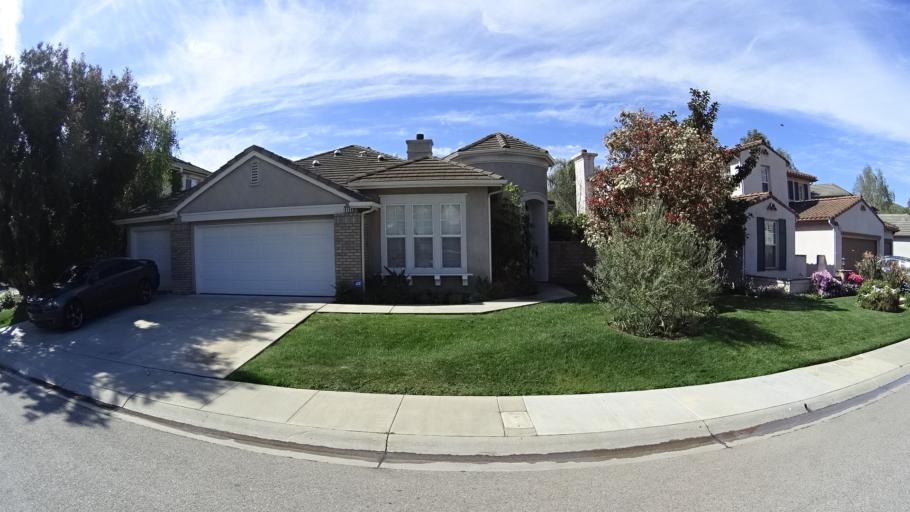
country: US
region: California
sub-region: Ventura County
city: Casa Conejo
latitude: 34.1712
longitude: -118.9660
